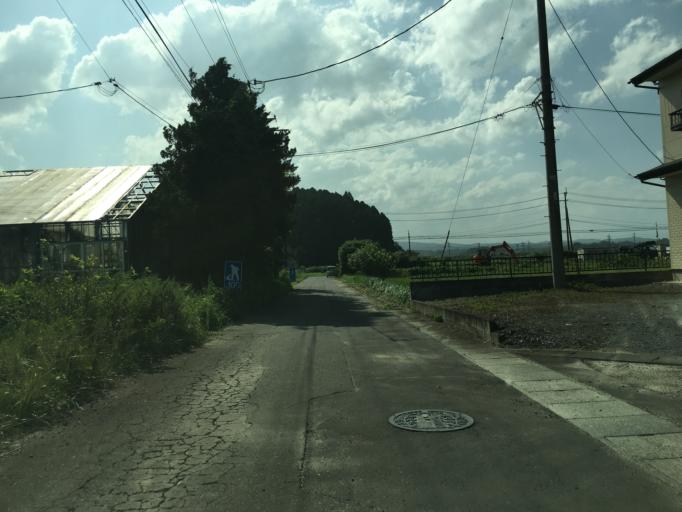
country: JP
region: Miyagi
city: Kakuda
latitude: 37.9584
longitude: 140.7822
